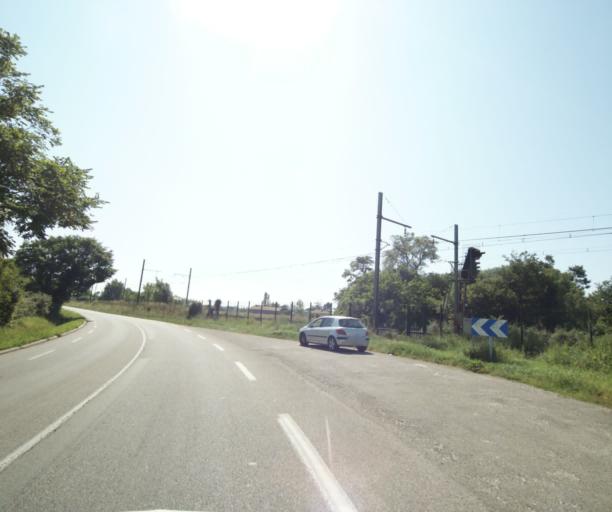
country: FR
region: Midi-Pyrenees
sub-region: Departement du Tarn-et-Garonne
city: Montbeton
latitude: 44.0154
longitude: 1.3117
